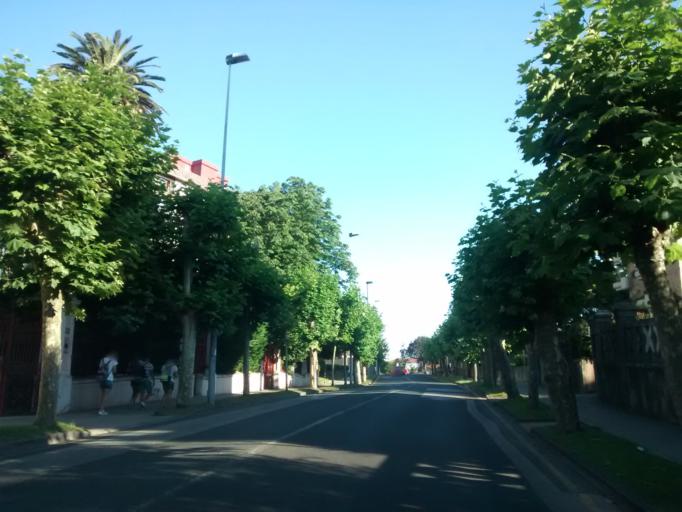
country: ES
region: Cantabria
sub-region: Provincia de Cantabria
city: Santander
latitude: 43.4709
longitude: -3.7874
